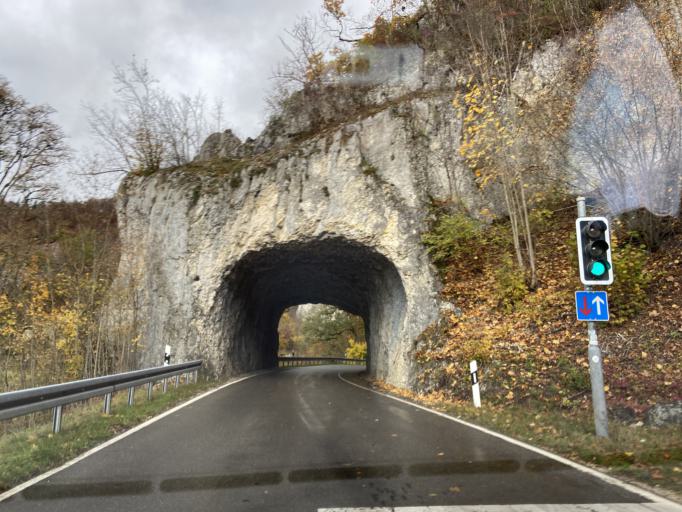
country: DE
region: Baden-Wuerttemberg
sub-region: Tuebingen Region
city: Stetten am Kalten Markt
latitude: 48.0923
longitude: 9.1081
